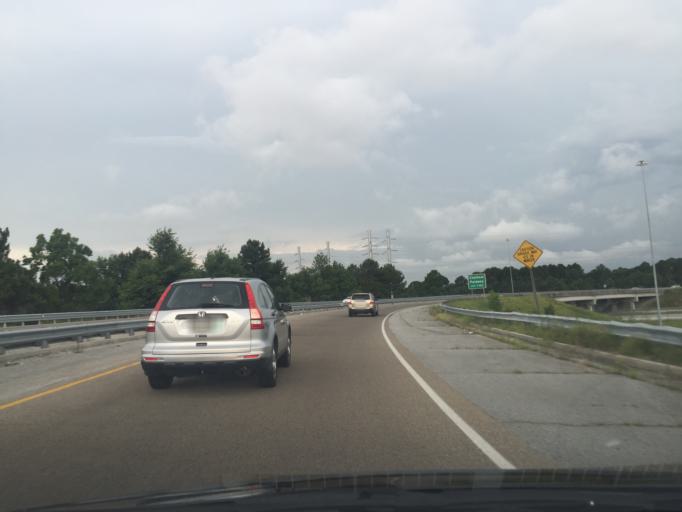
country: US
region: Georgia
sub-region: Chatham County
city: Savannah
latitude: 32.0437
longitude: -81.1450
